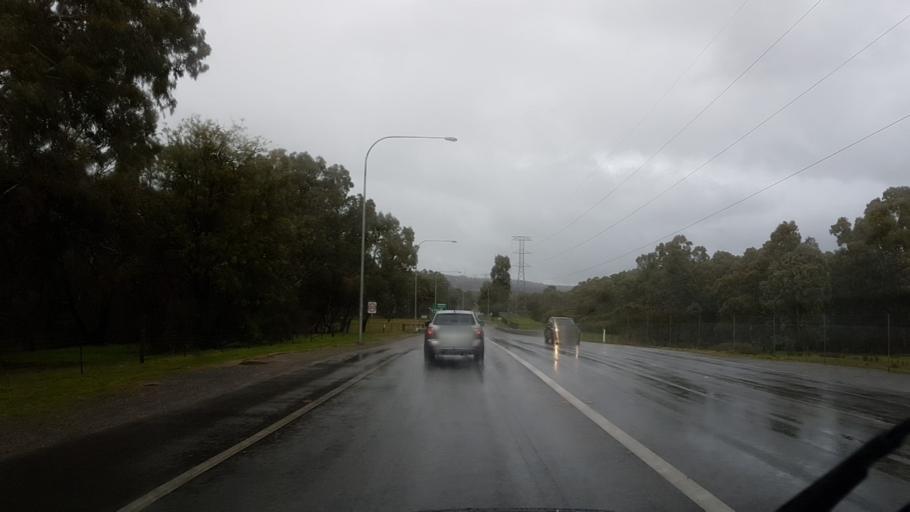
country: AU
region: South Australia
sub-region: Onkaparinga
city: Craigburn Farm
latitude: -35.0704
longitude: 138.5831
